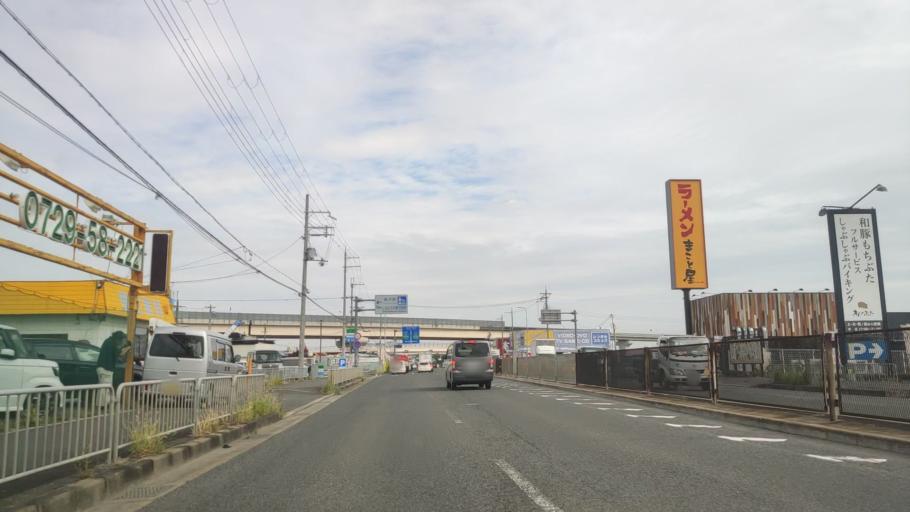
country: JP
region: Osaka
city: Tondabayashicho
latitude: 34.5316
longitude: 135.6048
